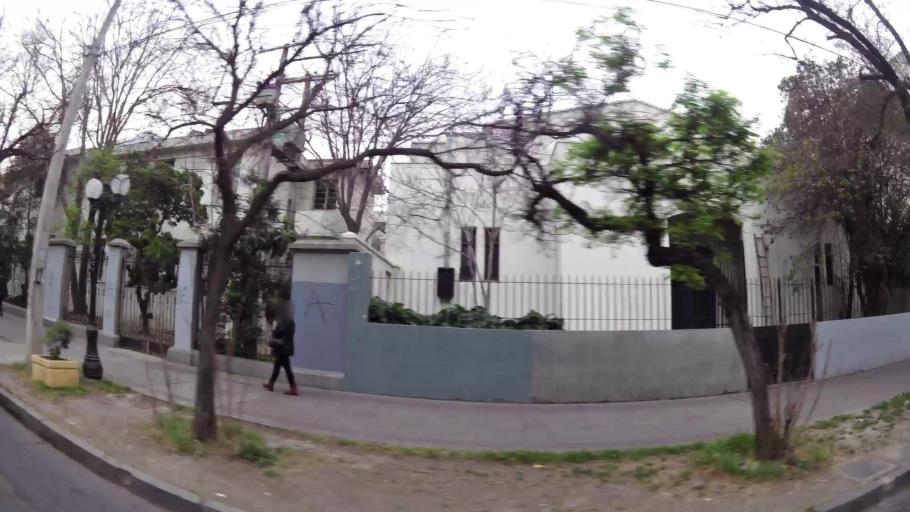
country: CL
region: Santiago Metropolitan
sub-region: Provincia de Santiago
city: Santiago
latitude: -33.4307
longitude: -70.6215
